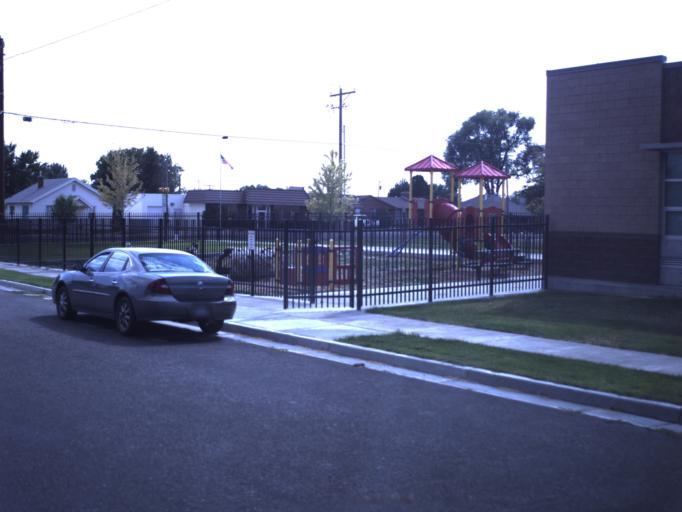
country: US
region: Utah
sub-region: Box Elder County
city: Garland
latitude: 41.8151
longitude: -112.1162
